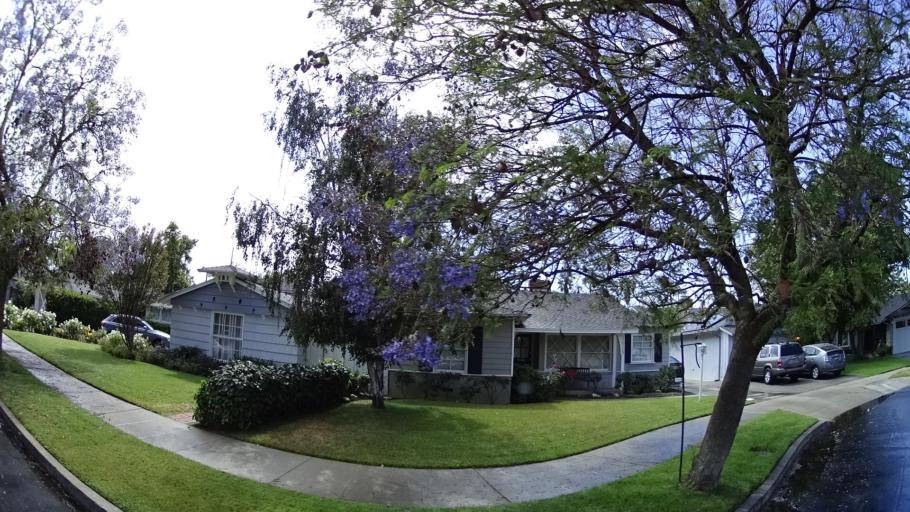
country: US
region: California
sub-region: Los Angeles County
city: Sherman Oaks
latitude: 34.1604
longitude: -118.4172
